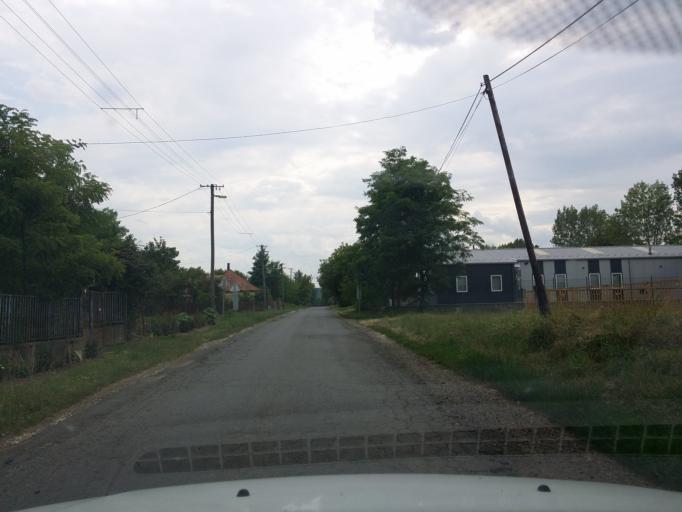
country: HU
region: Nograd
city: Romhany
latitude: 47.9724
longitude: 19.3574
